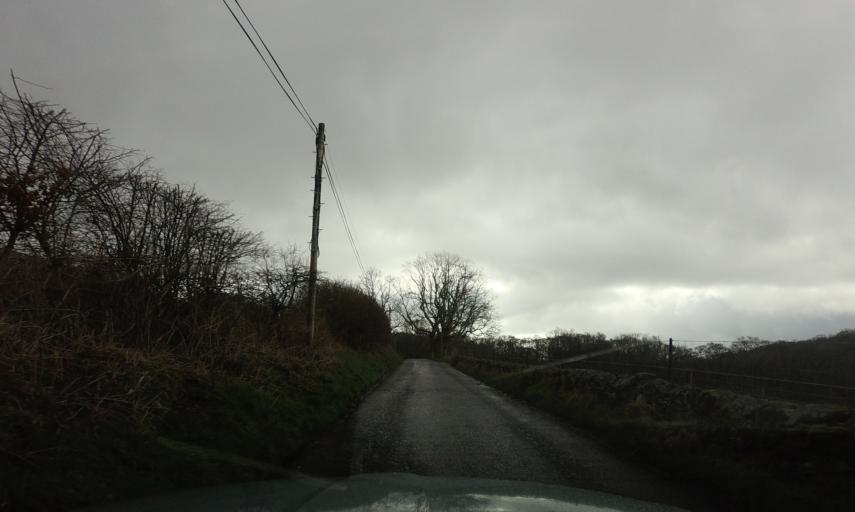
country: GB
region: Scotland
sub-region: West Dunbartonshire
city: Balloch
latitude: 56.1389
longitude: -4.6182
